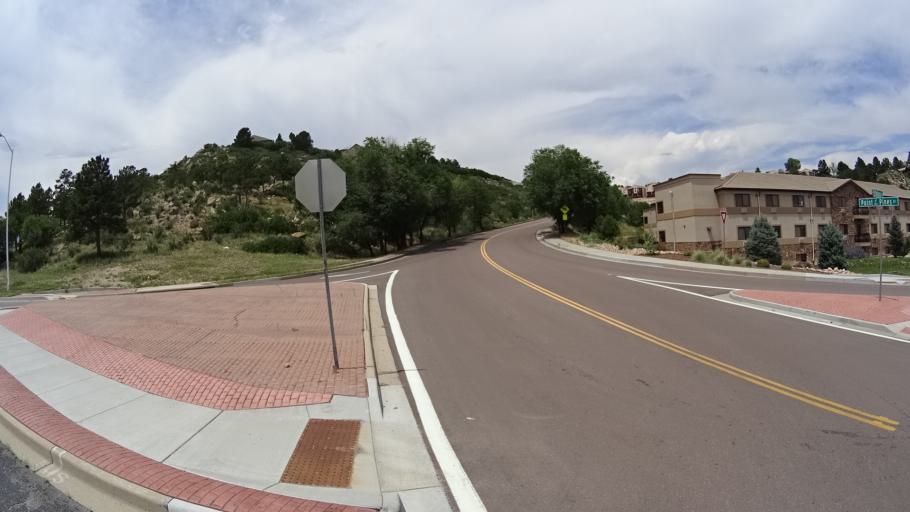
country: US
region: Colorado
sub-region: El Paso County
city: Colorado Springs
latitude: 38.9015
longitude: -104.8298
